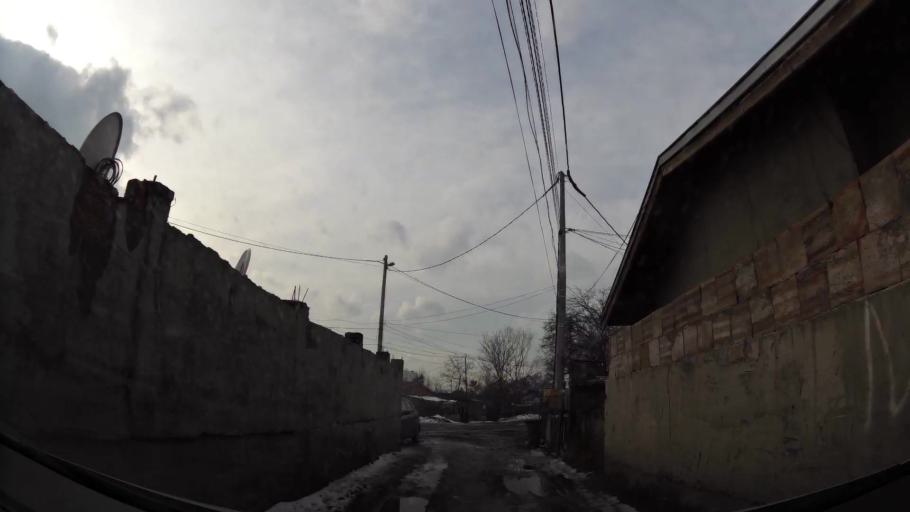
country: BG
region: Sofia-Capital
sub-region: Stolichna Obshtina
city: Sofia
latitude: 42.6943
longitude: 23.3817
